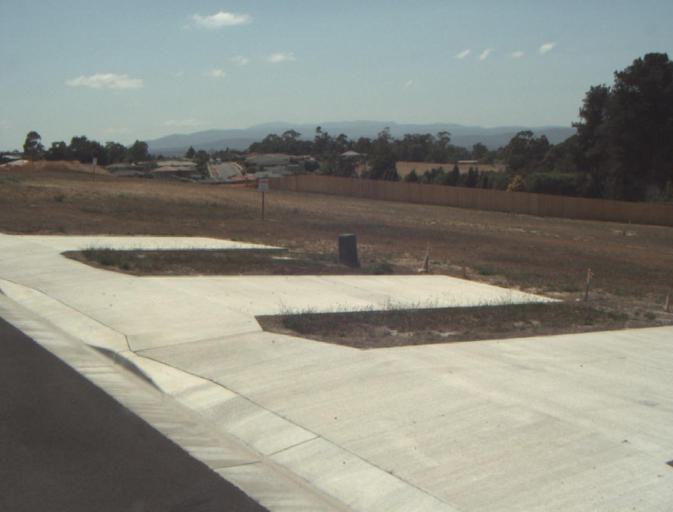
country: AU
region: Tasmania
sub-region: Launceston
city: Summerhill
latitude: -41.4918
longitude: 147.1697
